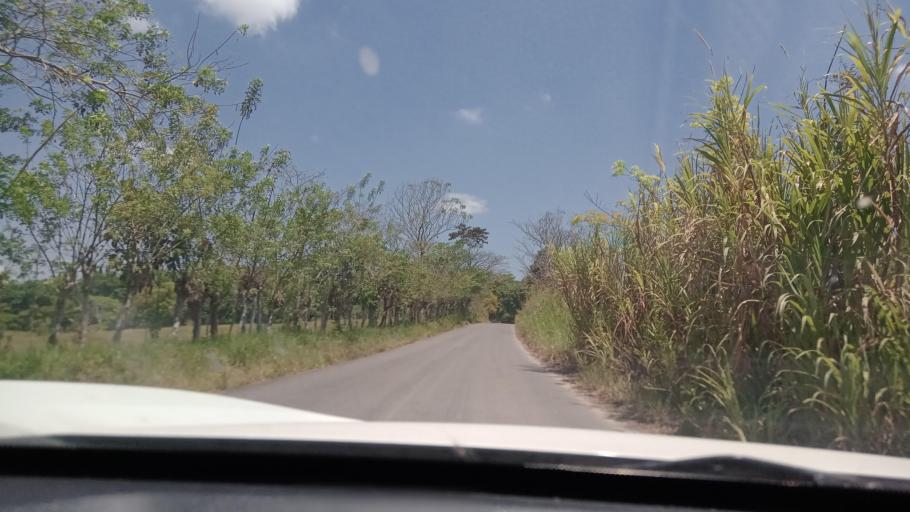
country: MX
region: Veracruz
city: Las Choapas
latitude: 17.7665
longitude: -94.1077
